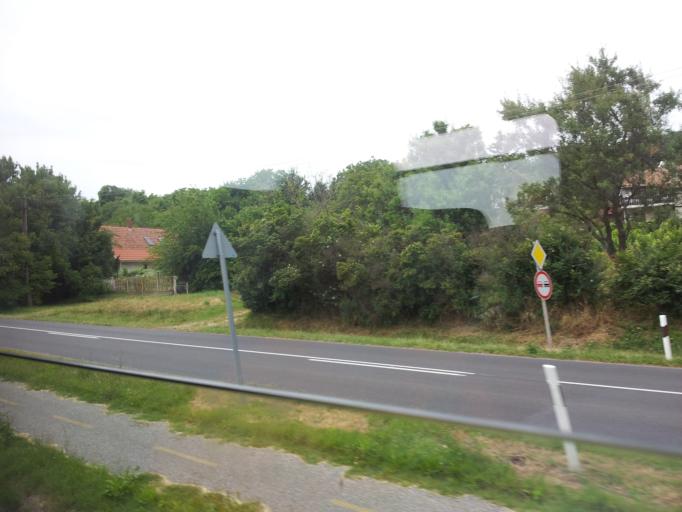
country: HU
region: Veszprem
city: Badacsonytomaj
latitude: 46.8079
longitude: 17.5565
